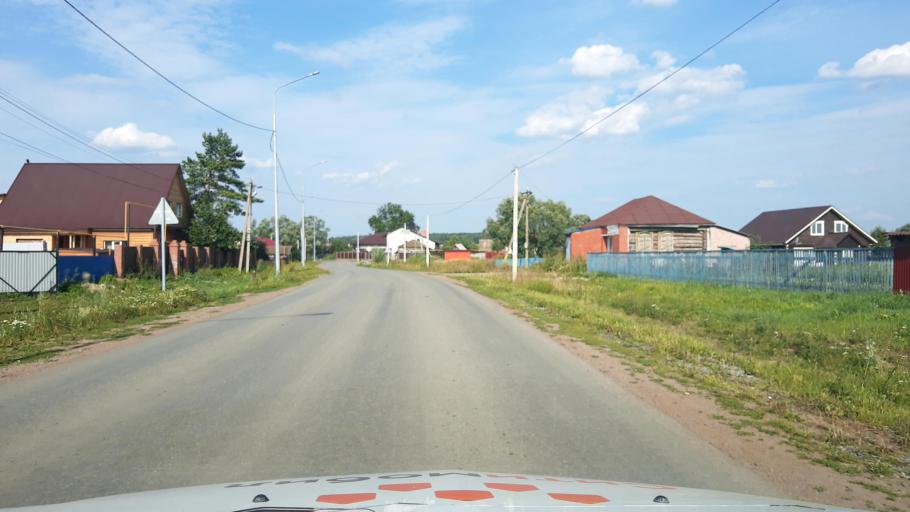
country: RU
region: Bashkortostan
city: Kabakovo
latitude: 54.6576
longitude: 56.1970
